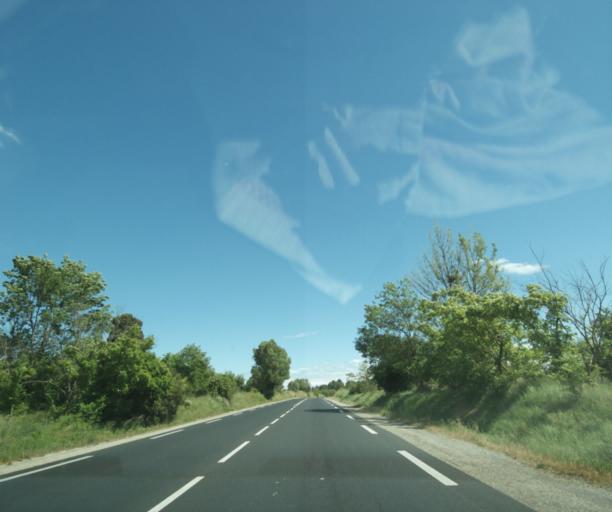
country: FR
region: Languedoc-Roussillon
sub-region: Departement de l'Herault
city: Saint-Jean-de-Vedas
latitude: 43.5882
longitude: 3.8248
